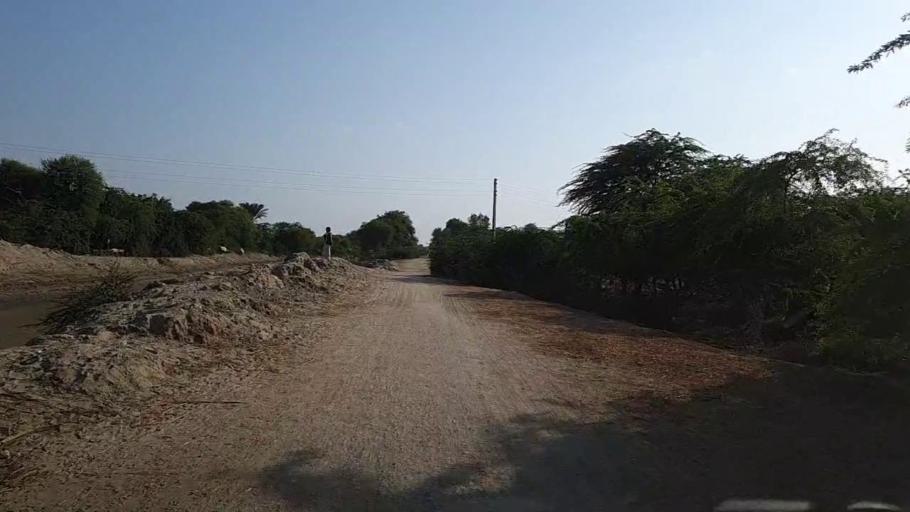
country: PK
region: Sindh
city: Kario
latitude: 24.7918
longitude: 68.6718
